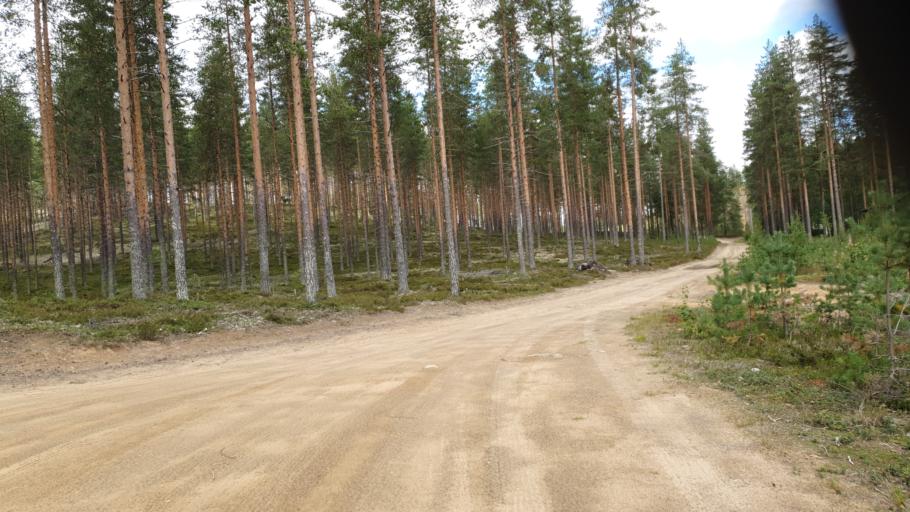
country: FI
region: Kainuu
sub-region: Kehys-Kainuu
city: Kuhmo
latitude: 64.1499
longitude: 29.3872
